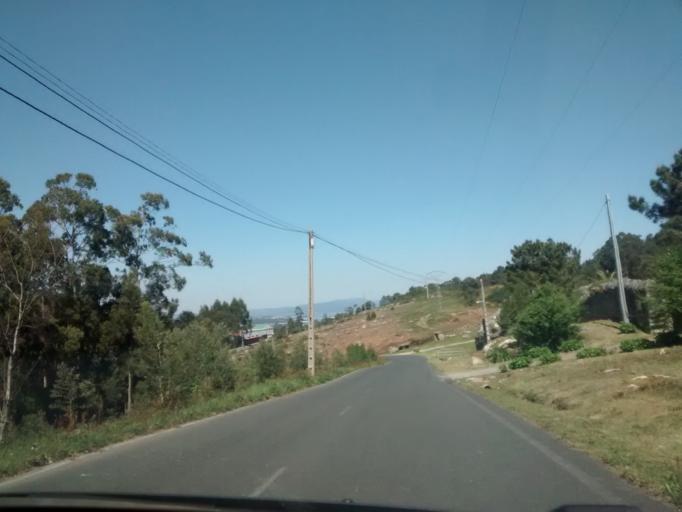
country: ES
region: Galicia
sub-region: Provincia de Pontevedra
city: O Grove
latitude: 42.4766
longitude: -8.8808
